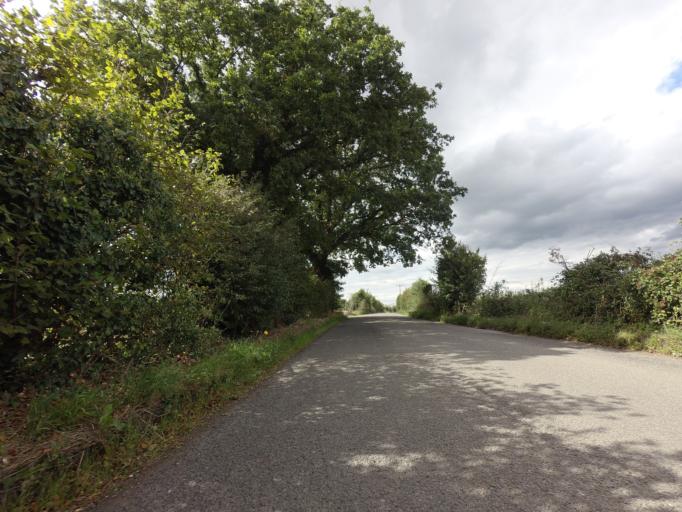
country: GB
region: England
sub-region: Kent
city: Paddock Wood
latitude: 51.1622
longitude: 0.4303
